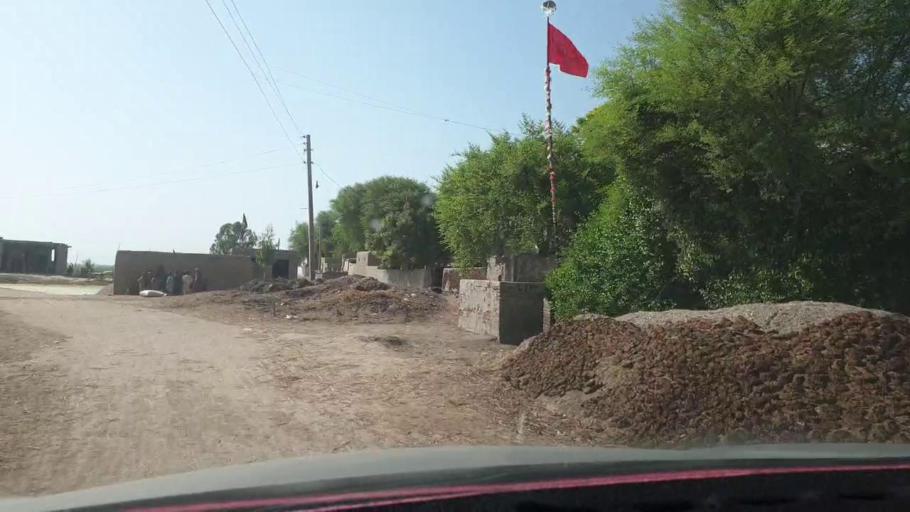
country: PK
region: Sindh
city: Nasirabad
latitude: 27.3843
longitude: 67.8774
